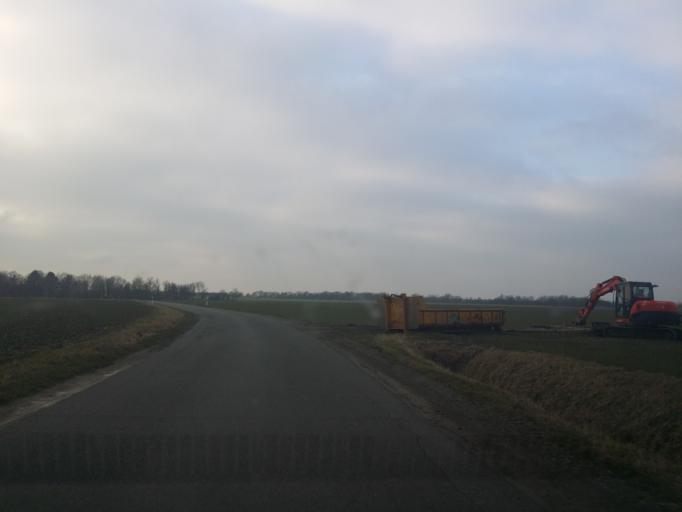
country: DE
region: Schleswig-Holstein
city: Grossenbrode
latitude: 54.4612
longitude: 11.0393
